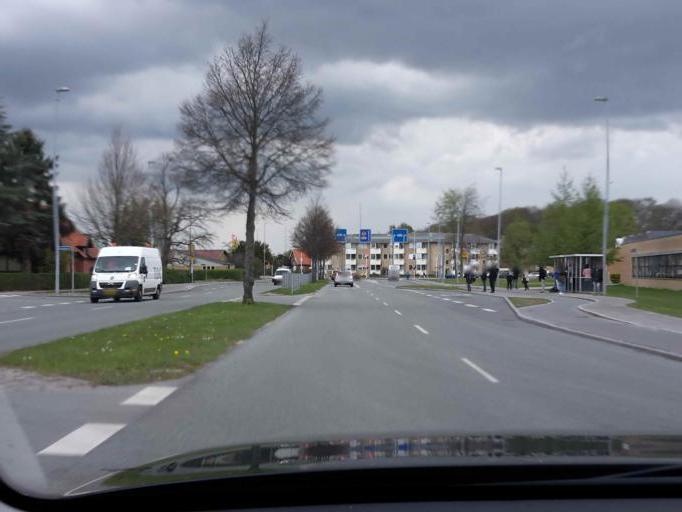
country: DK
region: South Denmark
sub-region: Odense Kommune
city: Odense
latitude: 55.3802
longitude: 10.4082
